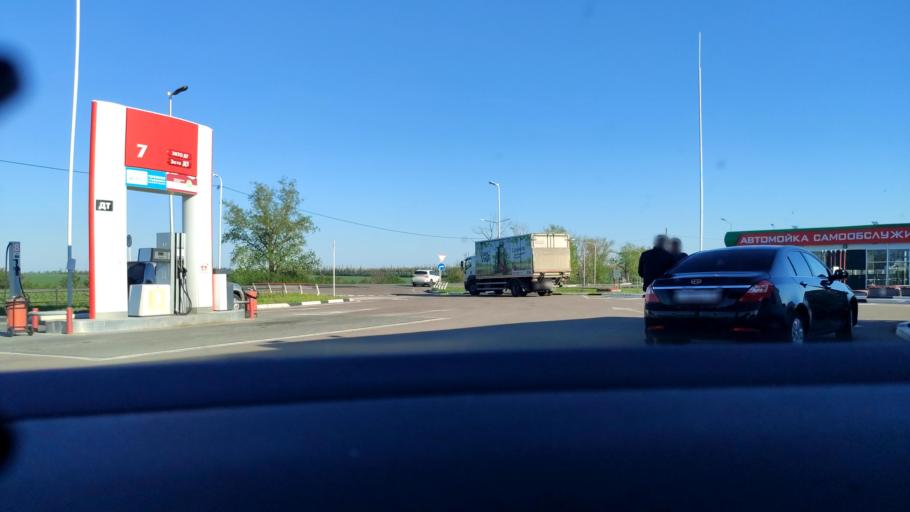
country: RU
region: Voronezj
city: Maslovka
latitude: 51.5069
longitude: 39.3055
